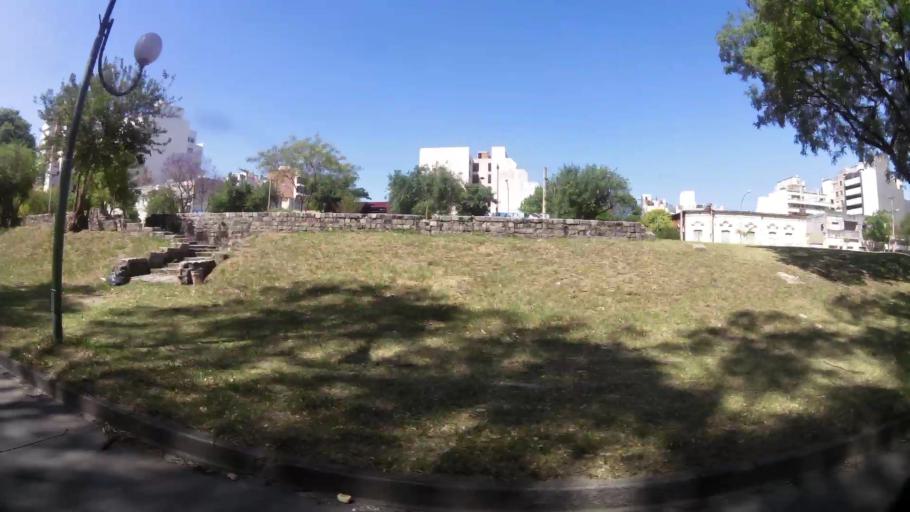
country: AR
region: Cordoba
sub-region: Departamento de Capital
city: Cordoba
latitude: -31.4169
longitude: -64.1733
